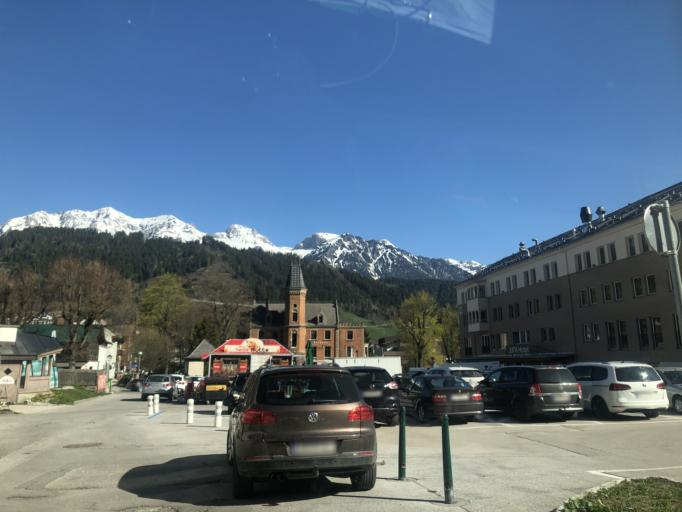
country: AT
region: Styria
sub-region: Politischer Bezirk Liezen
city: Schladming
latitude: 47.3916
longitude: 13.6905
